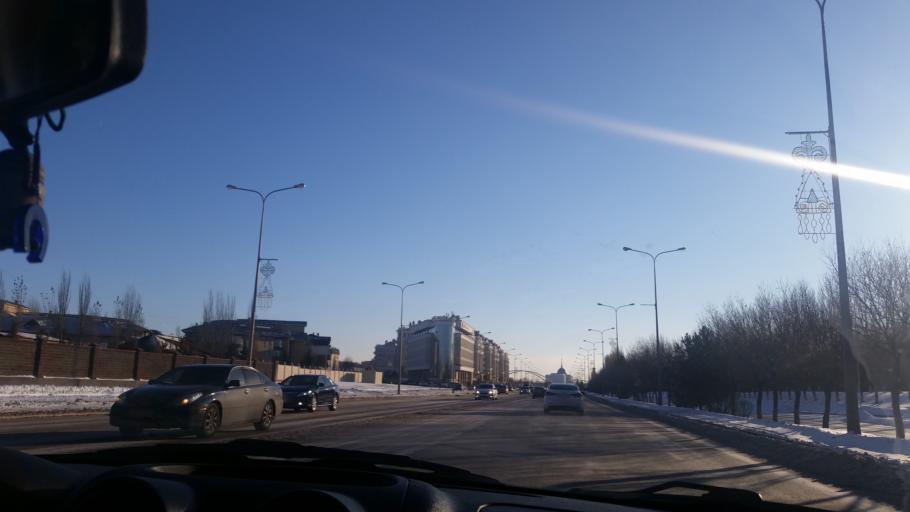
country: KZ
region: Astana Qalasy
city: Astana
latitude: 51.1474
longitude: 71.4447
